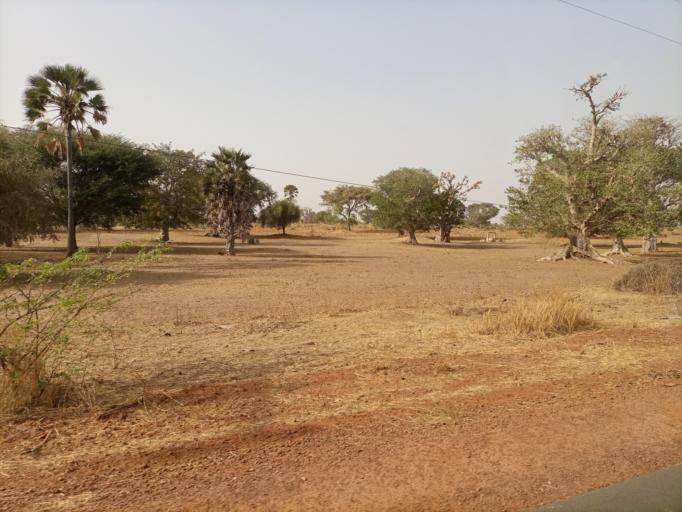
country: SN
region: Fatick
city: Foundiougne
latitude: 14.1195
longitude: -16.4450
